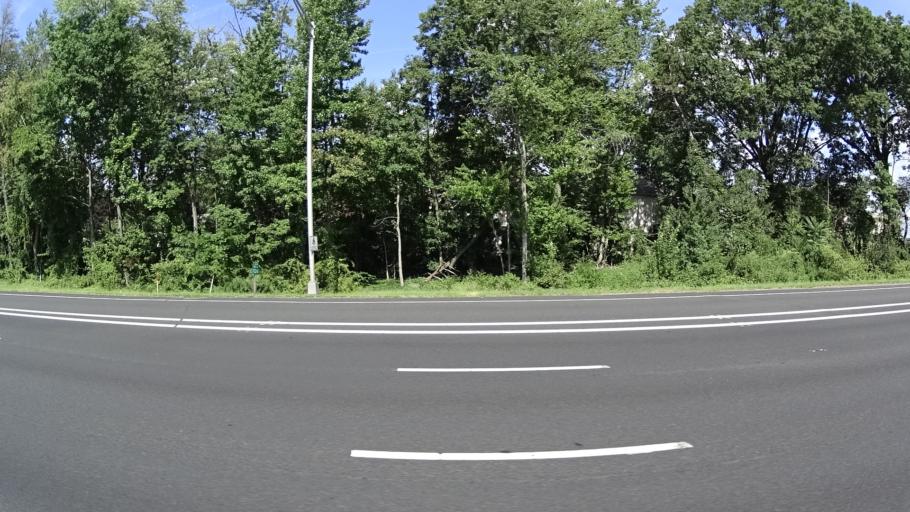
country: US
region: New Jersey
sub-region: Union County
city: Clark
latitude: 40.6255
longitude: -74.3062
